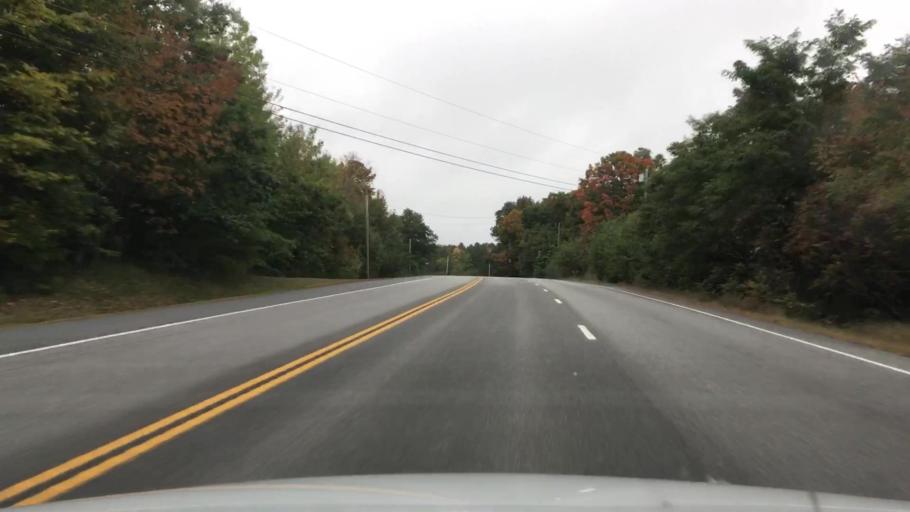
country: US
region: Maine
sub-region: Androscoggin County
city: Poland
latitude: 44.0858
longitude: -70.4203
